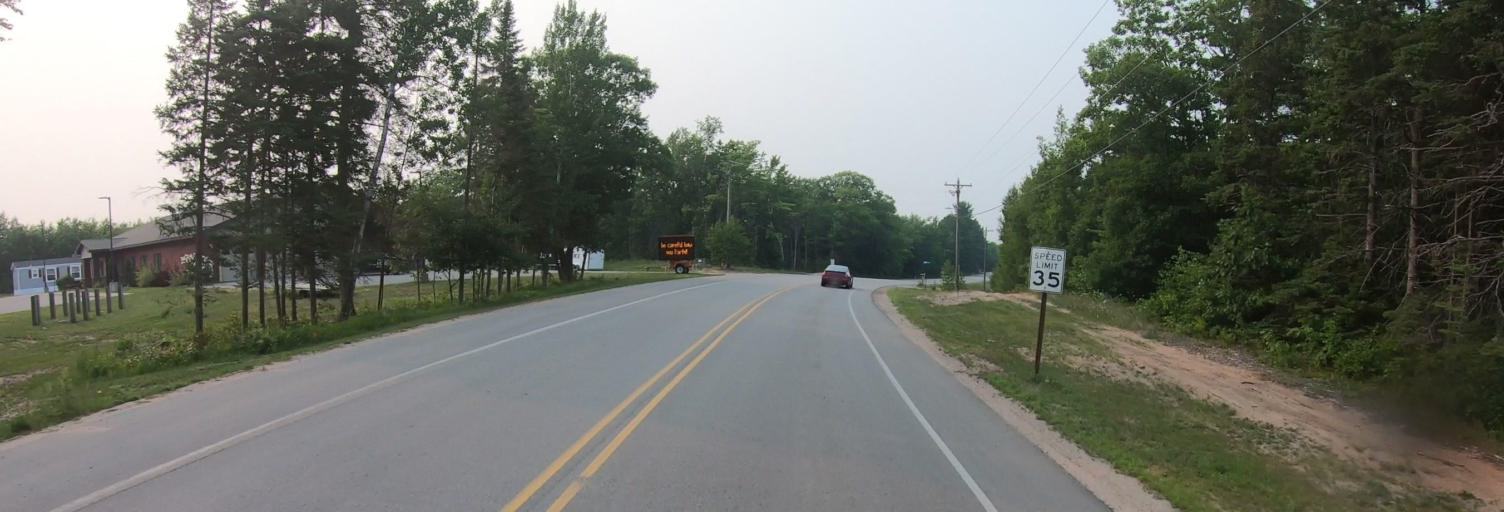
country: US
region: Michigan
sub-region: Chippewa County
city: Sault Ste. Marie
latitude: 46.4616
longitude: -84.6184
